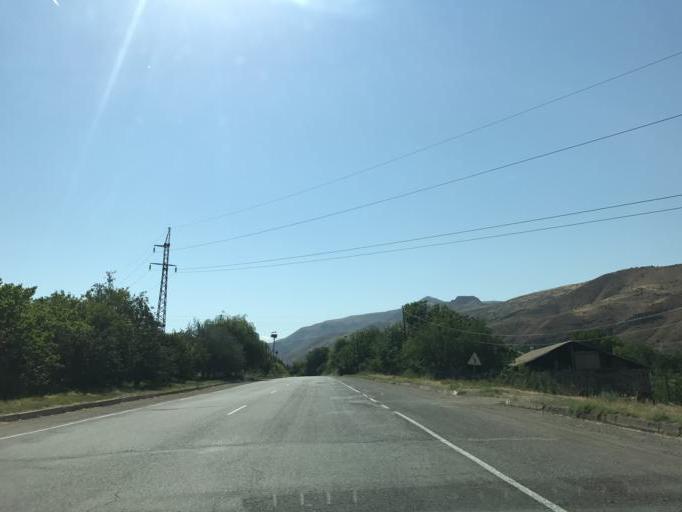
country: AM
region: Vayots' Dzori Marz
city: Getap'
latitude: 39.7375
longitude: 45.2691
